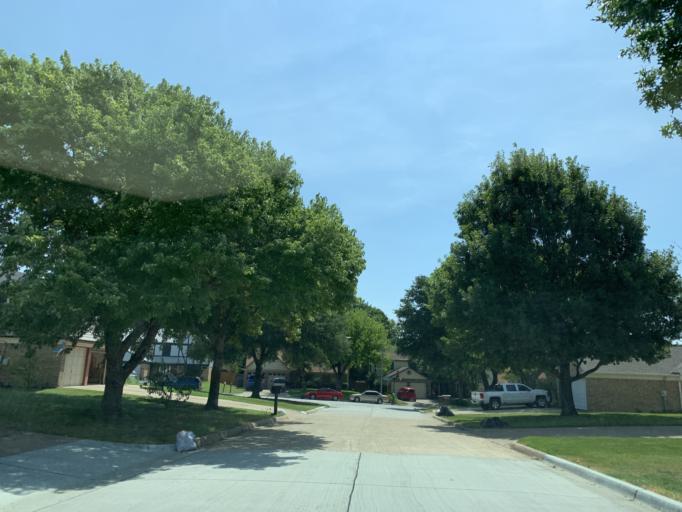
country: US
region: Texas
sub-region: Dallas County
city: Grand Prairie
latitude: 32.6670
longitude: -97.0334
